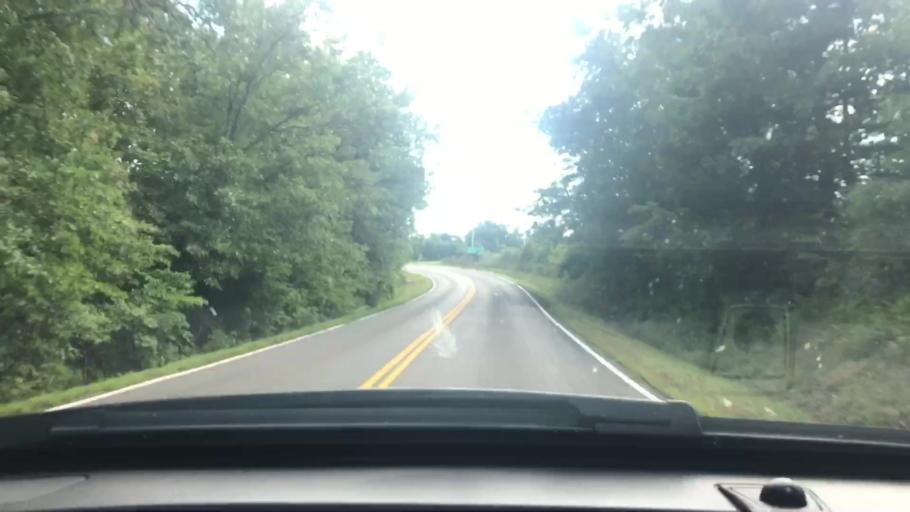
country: US
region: Missouri
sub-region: Wright County
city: Mountain Grove
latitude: 37.3027
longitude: -92.3126
